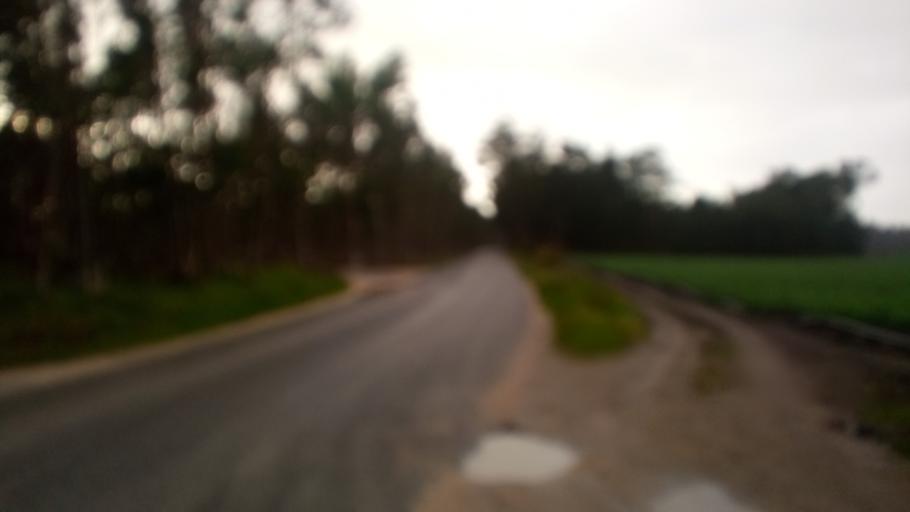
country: PT
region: Leiria
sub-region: Caldas da Rainha
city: Caldas da Rainha
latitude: 39.4406
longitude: -9.1588
